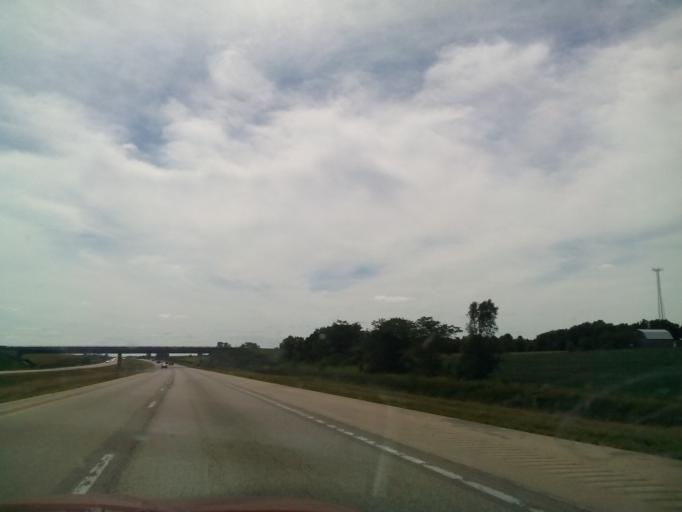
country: US
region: Illinois
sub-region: Ogle County
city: Davis Junction
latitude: 42.0456
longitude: -89.0209
